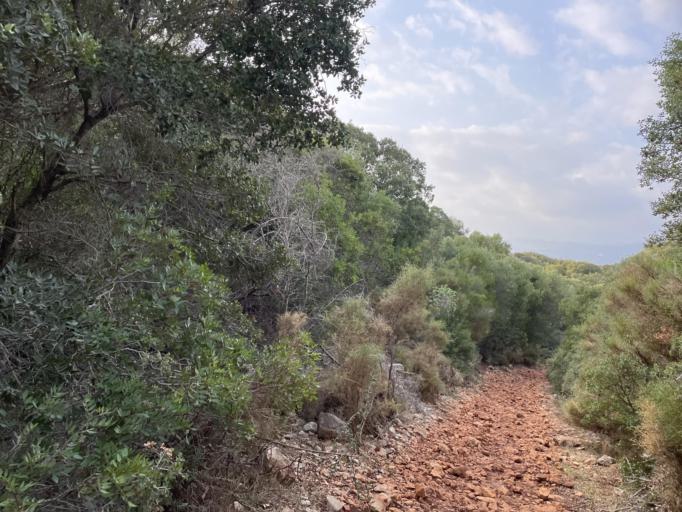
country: TR
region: Antalya
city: Kas
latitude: 36.1644
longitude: 29.6540
